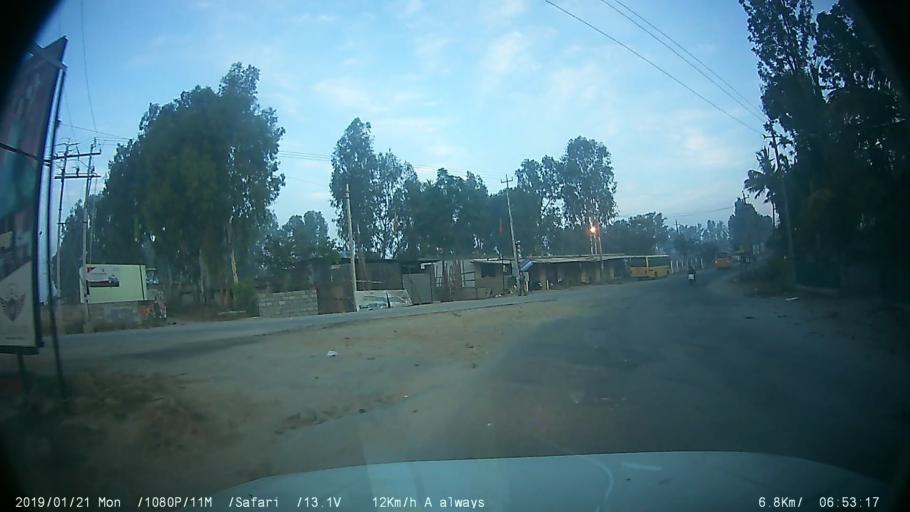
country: IN
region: Karnataka
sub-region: Bangalore Urban
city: Anekal
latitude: 12.8213
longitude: 77.6228
